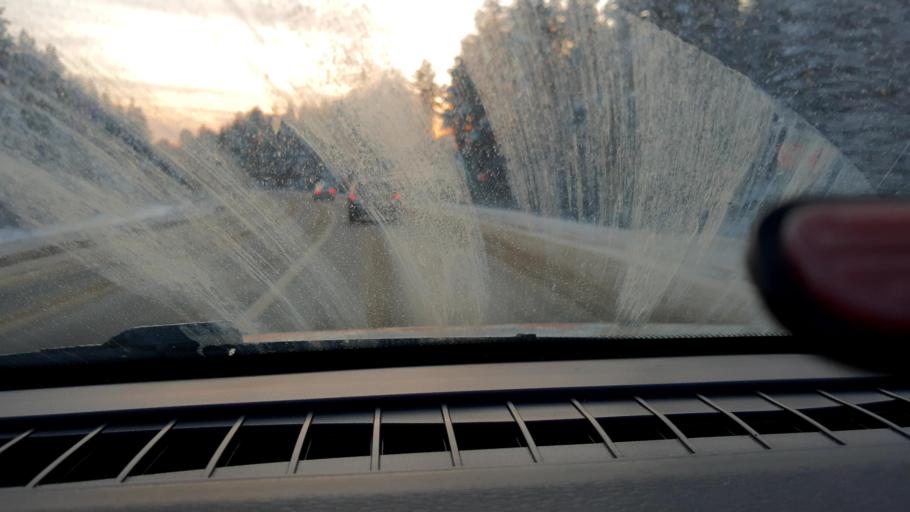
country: RU
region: Nizjnij Novgorod
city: Krasnyye Baki
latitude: 57.2113
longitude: 45.4645
